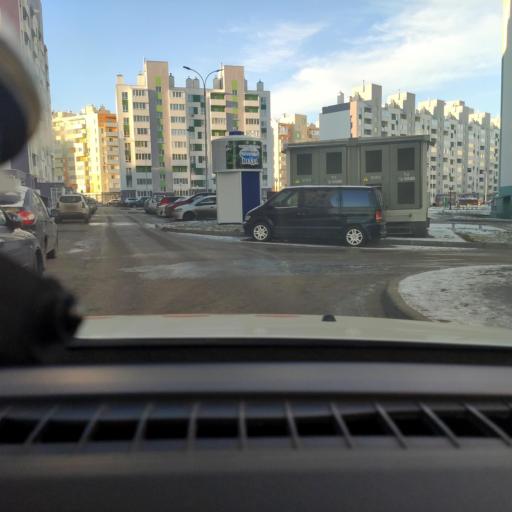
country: RU
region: Samara
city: Samara
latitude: 53.0959
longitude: 50.1663
